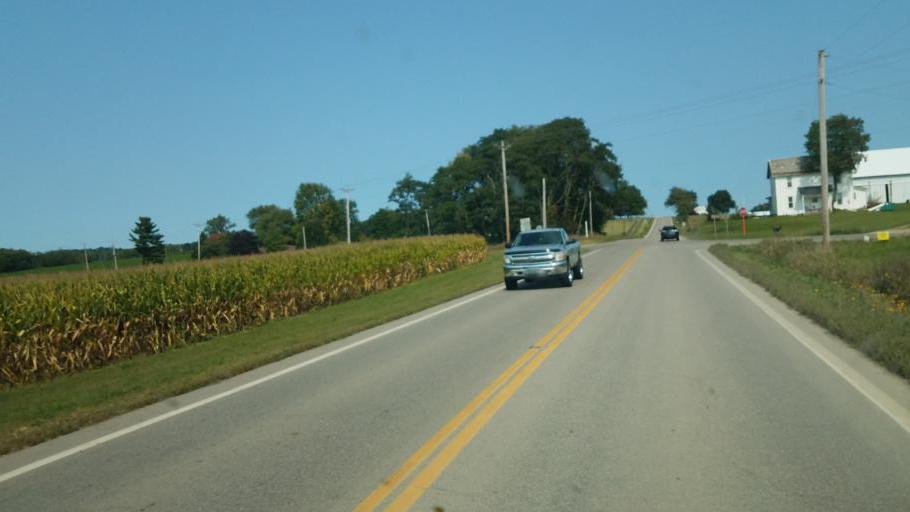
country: US
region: Ohio
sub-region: Wayne County
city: Shreve
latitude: 40.7241
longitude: -82.0540
